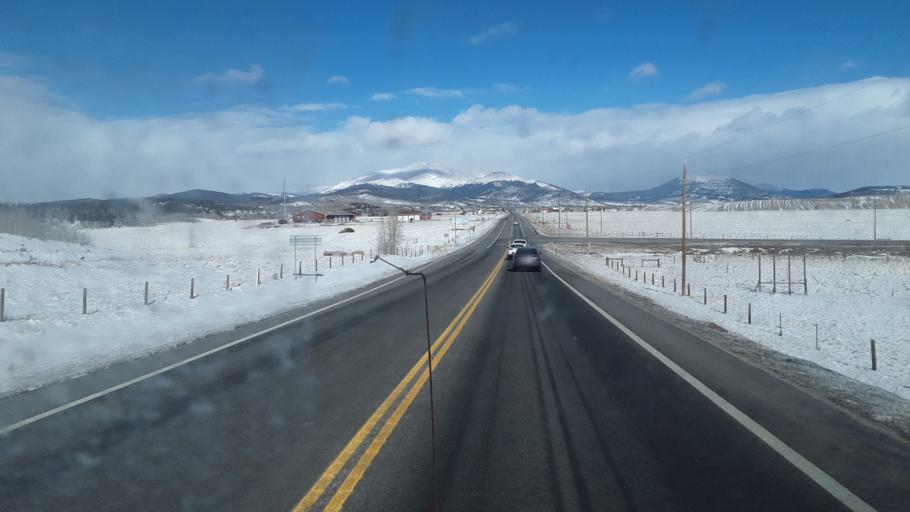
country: US
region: Colorado
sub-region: Park County
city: Fairplay
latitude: 39.2048
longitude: -105.9950
